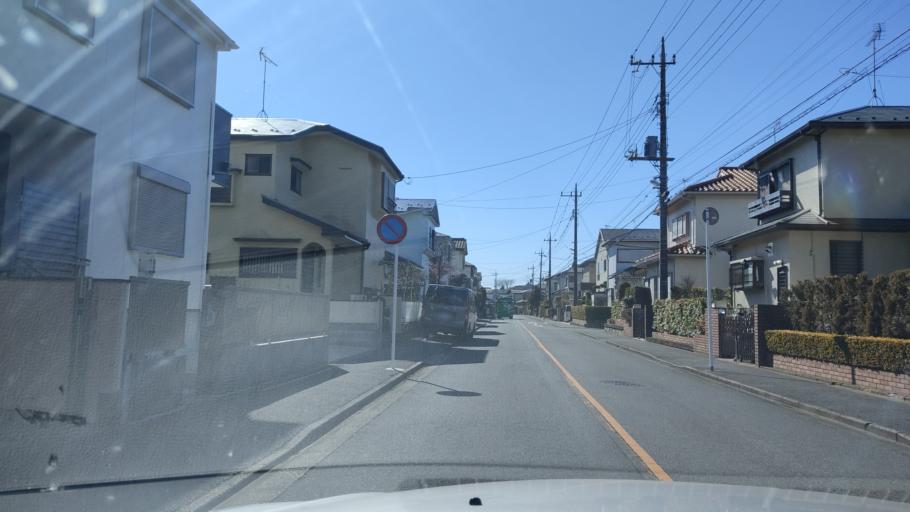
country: JP
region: Chiba
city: Nagareyama
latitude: 35.9099
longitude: 139.9178
